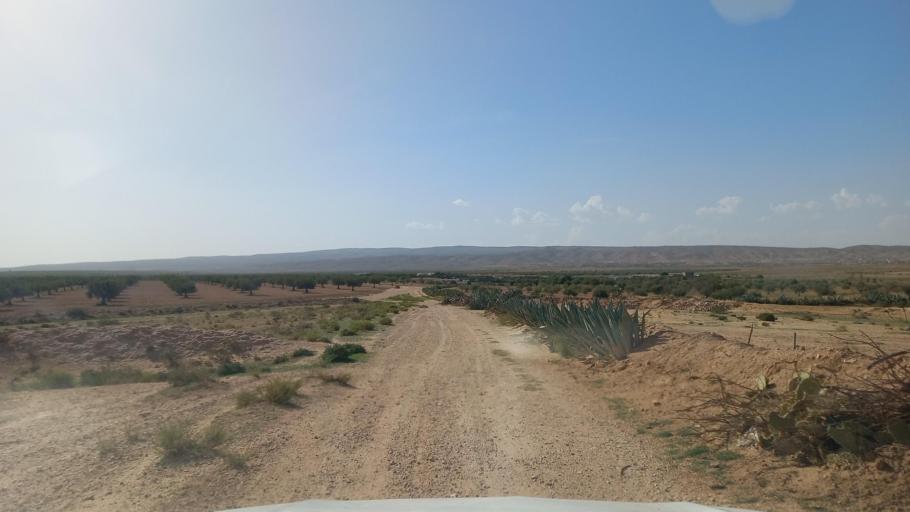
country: TN
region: Al Qasrayn
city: Kasserine
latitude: 35.3131
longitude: 9.0178
